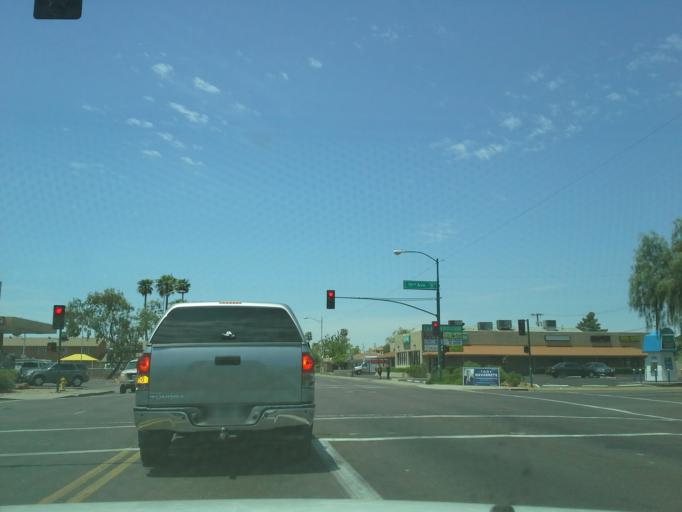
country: US
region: Arizona
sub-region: Maricopa County
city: Phoenix
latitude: 33.4658
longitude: -112.0910
